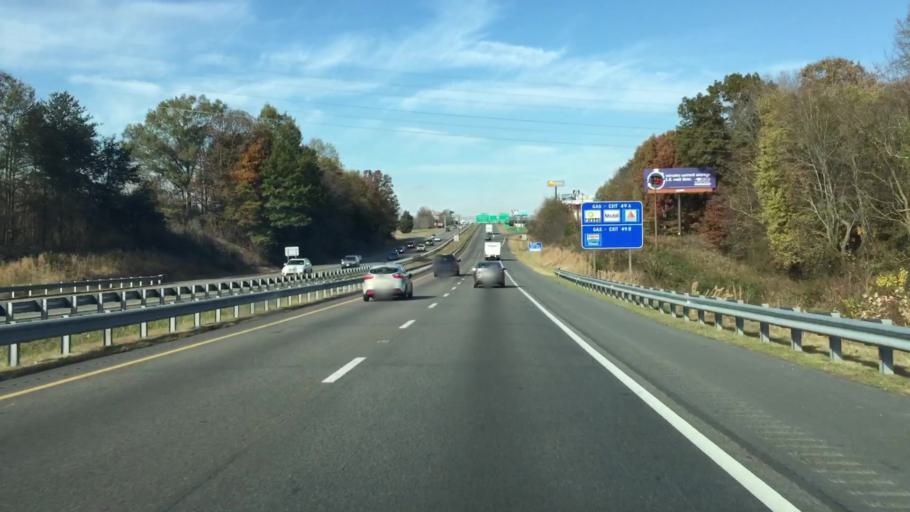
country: US
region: North Carolina
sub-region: Iredell County
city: Statesville
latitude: 35.7662
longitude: -80.8623
